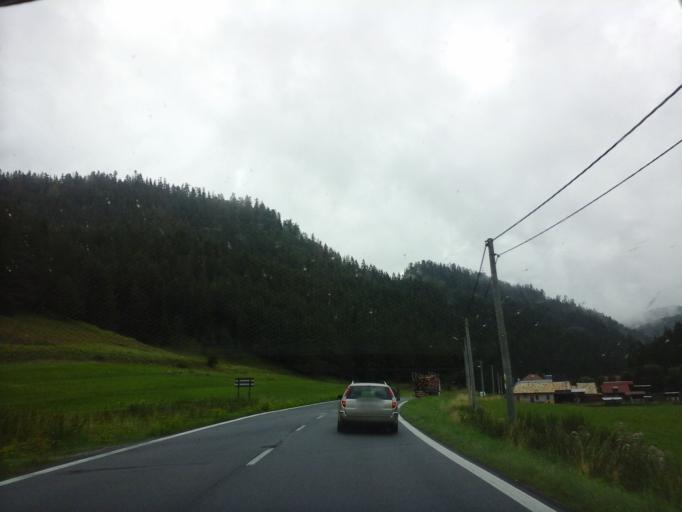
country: SK
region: Kosicky
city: Dobsina
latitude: 48.9215
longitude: 20.2730
